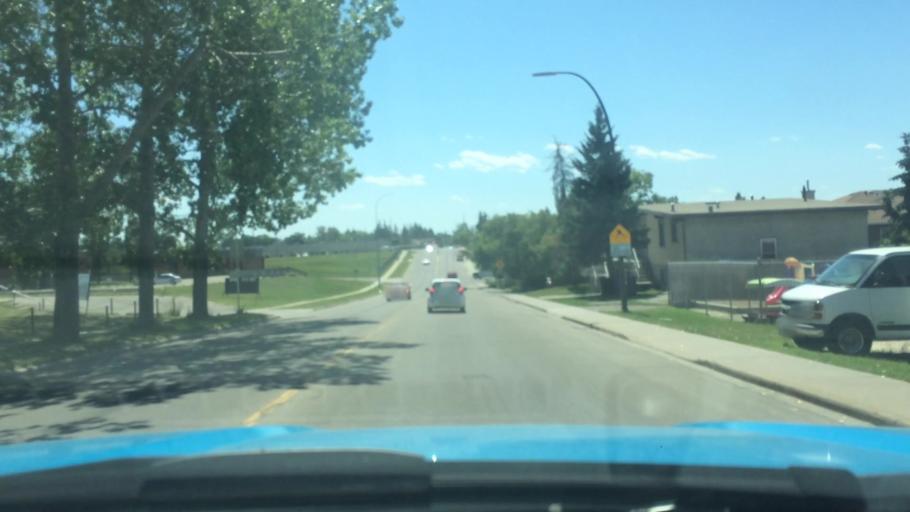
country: CA
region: Alberta
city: Calgary
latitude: 51.0419
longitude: -113.9931
